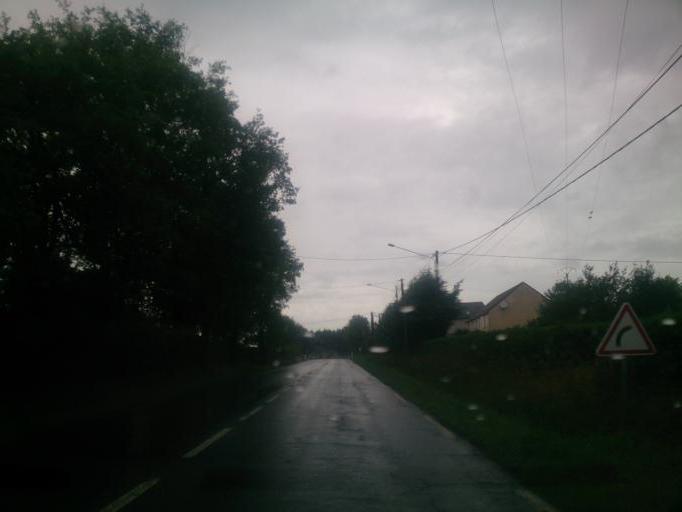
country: FR
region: Limousin
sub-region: Departement de la Correze
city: Sainte-Fereole
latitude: 45.1964
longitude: 1.5801
